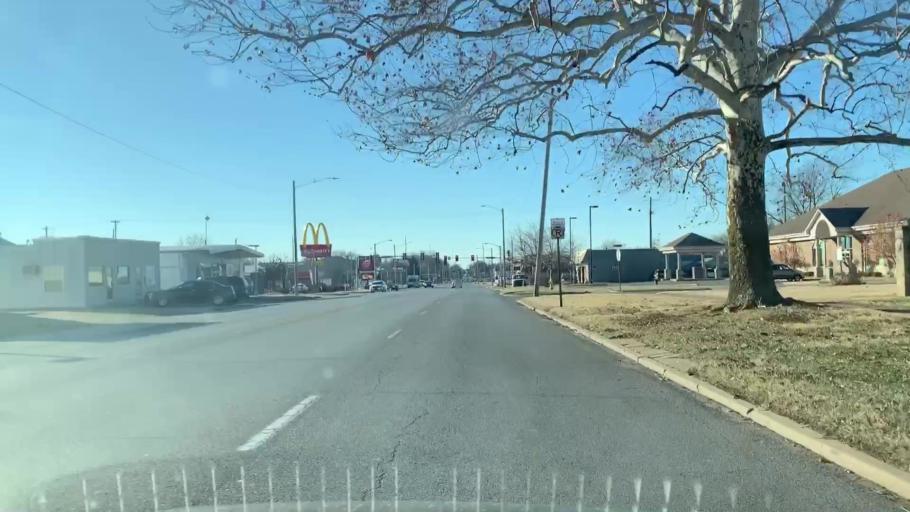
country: US
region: Kansas
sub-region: Crawford County
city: Pittsburg
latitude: 37.3978
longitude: -94.7050
